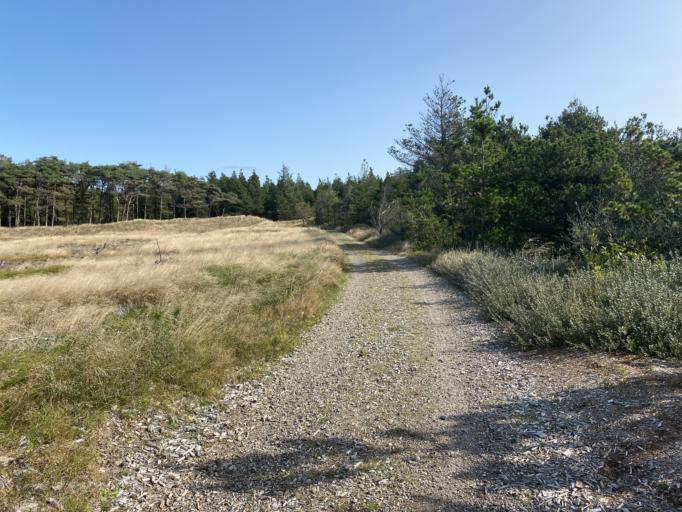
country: DK
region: Central Jutland
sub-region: Holstebro Kommune
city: Ulfborg
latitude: 56.2916
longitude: 8.1489
